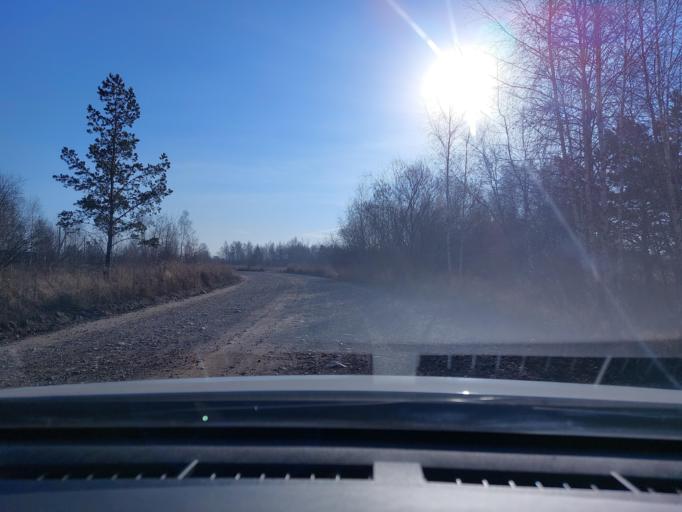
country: RU
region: Irkutsk
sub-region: Irkutskiy Rayon
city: Irkutsk
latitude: 52.3075
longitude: 104.2719
